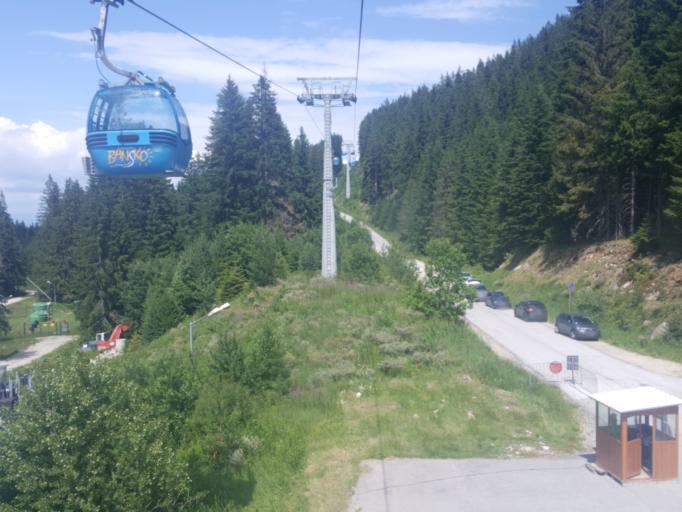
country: BG
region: Blagoevgrad
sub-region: Obshtina Bansko
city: Bansko
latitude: 41.7816
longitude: 23.4401
